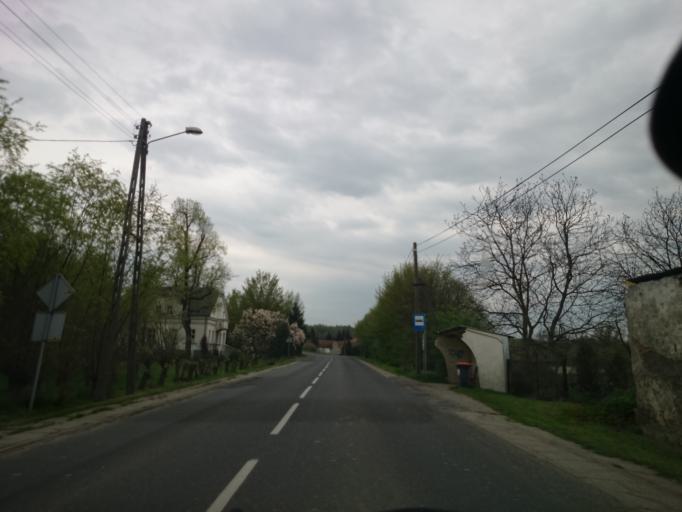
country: PL
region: Opole Voivodeship
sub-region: Powiat nyski
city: Glucholazy
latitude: 50.3868
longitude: 17.3500
